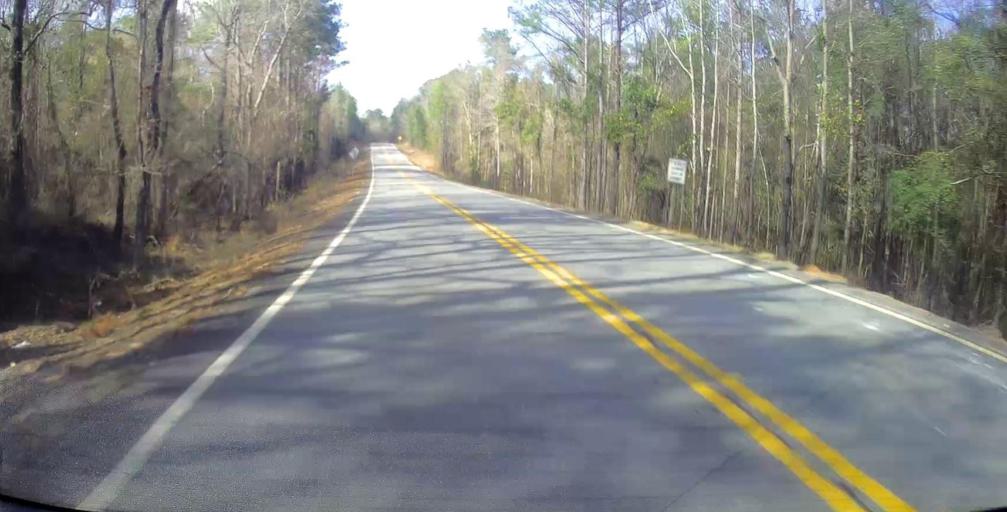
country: US
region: Georgia
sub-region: Wilkinson County
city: Gordon
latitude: 32.7863
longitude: -83.3302
